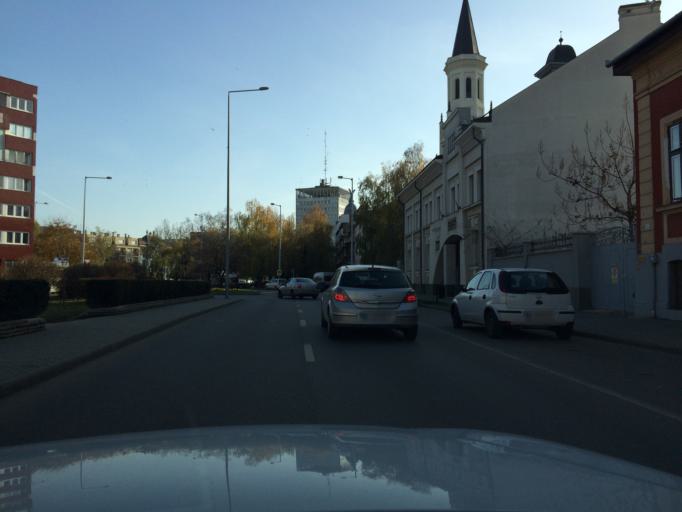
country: HU
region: Szabolcs-Szatmar-Bereg
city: Nyiregyhaza
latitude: 47.9548
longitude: 21.7137
